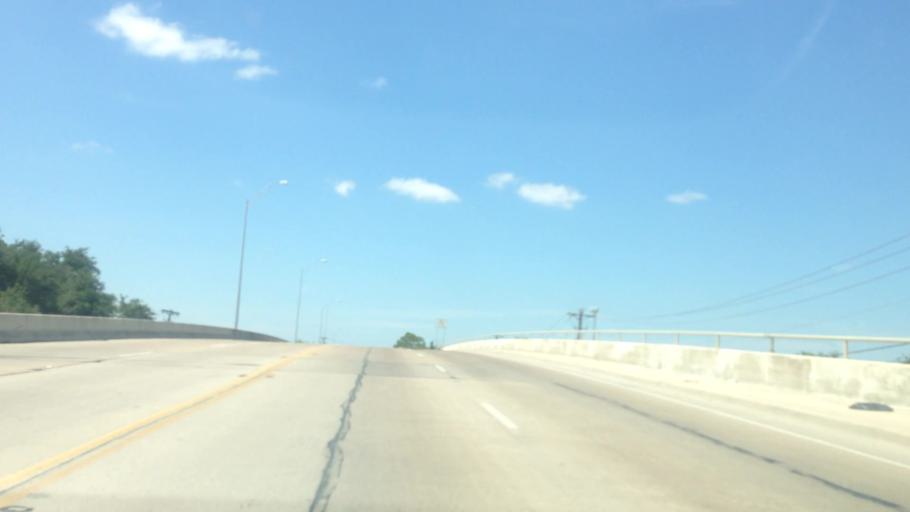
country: US
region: Texas
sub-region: Tarrant County
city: Haltom City
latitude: 32.7952
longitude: -97.3143
